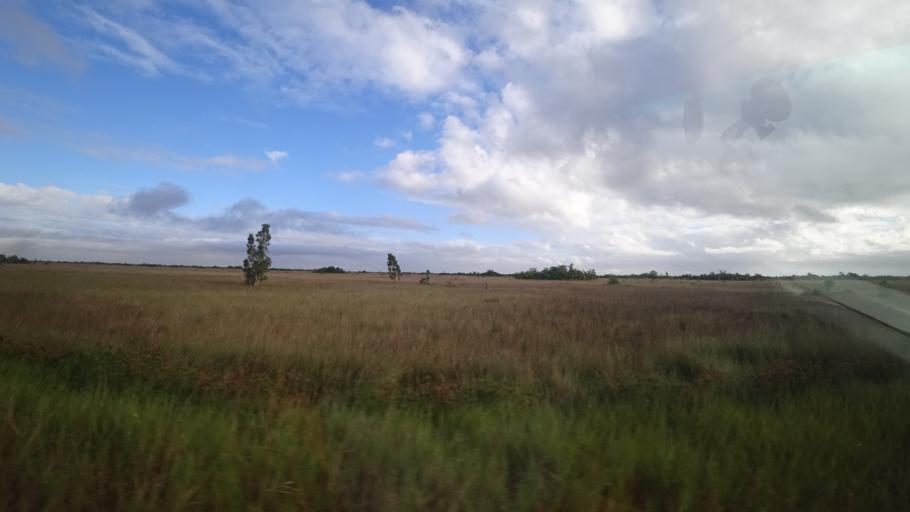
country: MZ
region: Sofala
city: Beira
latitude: -19.6936
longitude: 35.0371
